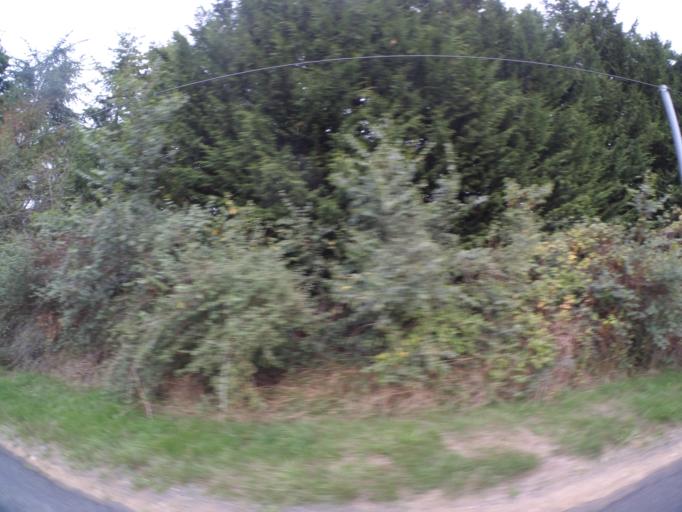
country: FR
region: Centre
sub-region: Departement d'Indre-et-Loire
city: Poce-sur-Cisse
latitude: 47.4894
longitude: 0.9817
